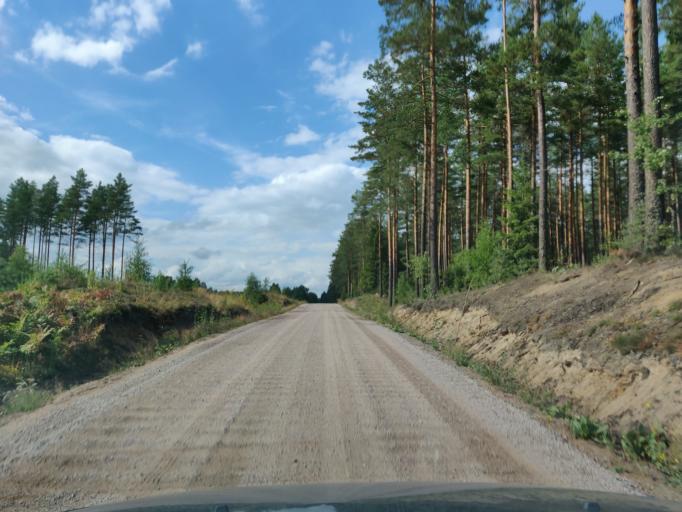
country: SE
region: Vaermland
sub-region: Munkfors Kommun
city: Munkfors
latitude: 59.9748
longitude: 13.5366
